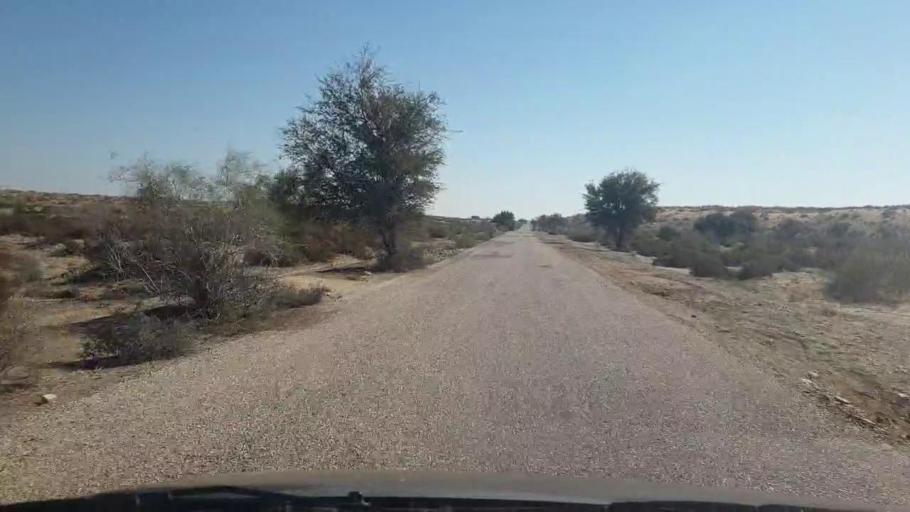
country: PK
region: Sindh
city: Bozdar
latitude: 27.0388
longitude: 68.6922
